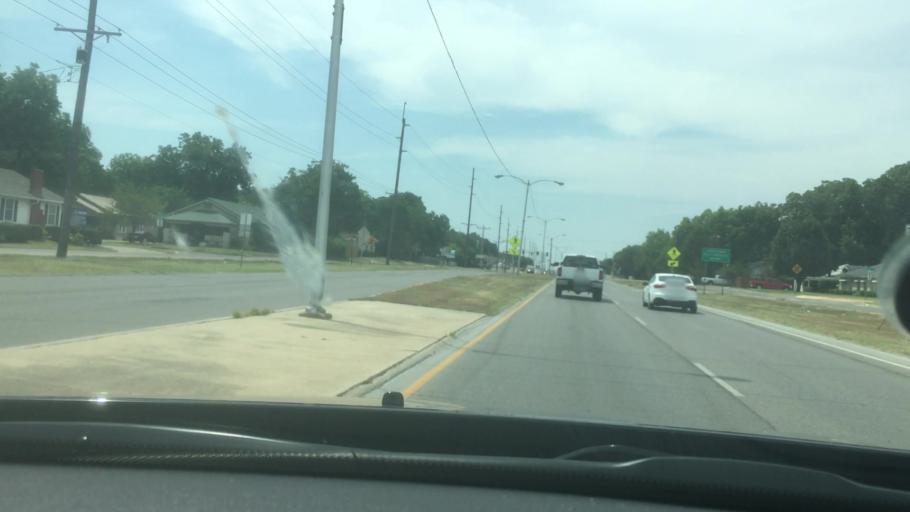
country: US
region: Oklahoma
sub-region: Carter County
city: Ardmore
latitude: 34.1739
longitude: -97.1434
